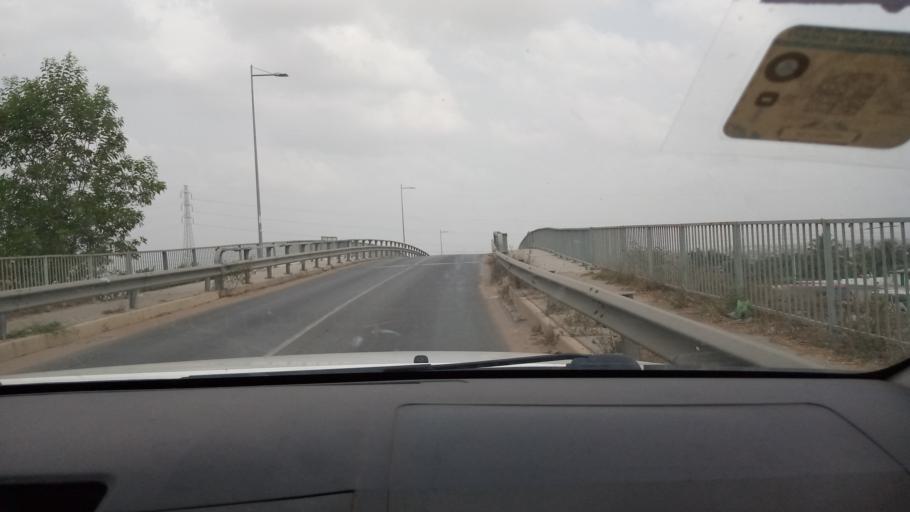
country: GH
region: Central
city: Kasoa
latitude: 5.5284
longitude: -0.4490
